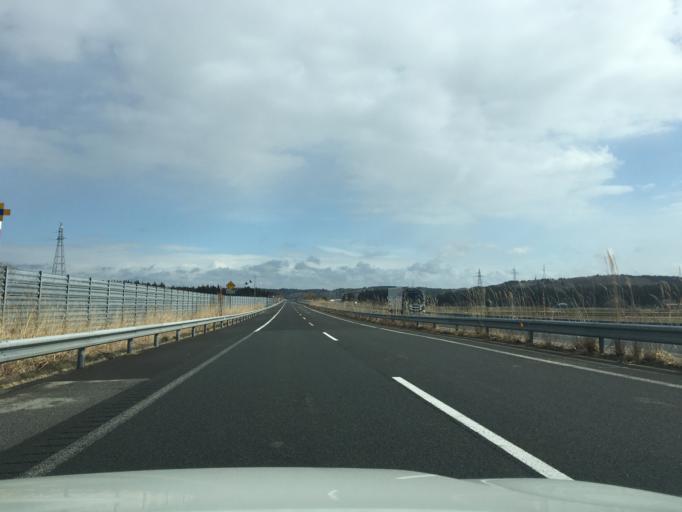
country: JP
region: Akita
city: Akita
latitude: 39.6150
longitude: 140.1438
